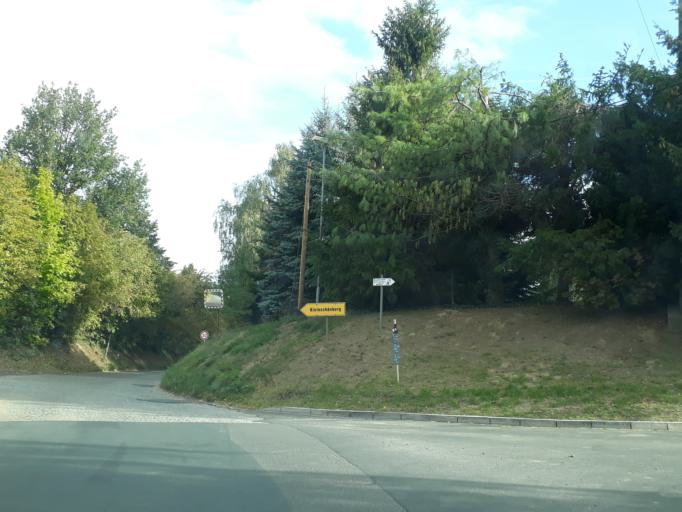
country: DE
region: Saxony
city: Coswig
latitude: 51.0837
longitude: 13.5825
